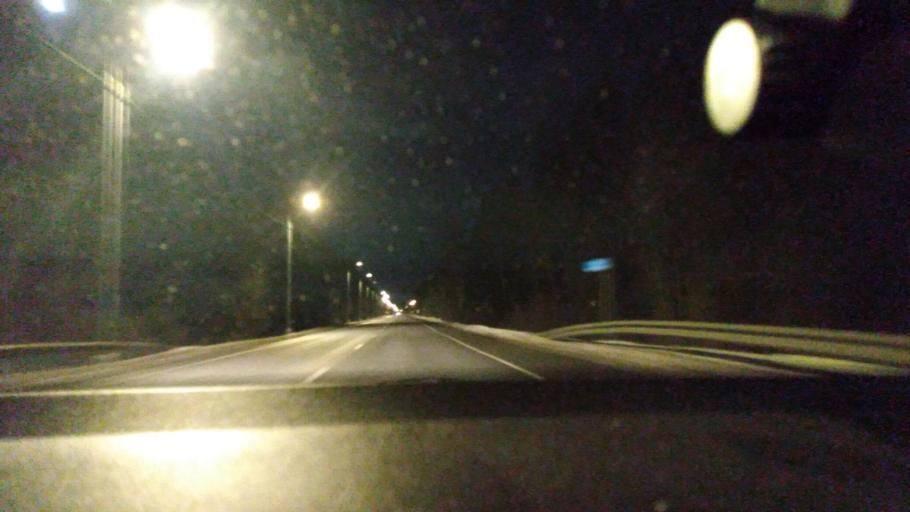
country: RU
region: Moskovskaya
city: Il'inskiy Pogost
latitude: 55.4625
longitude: 38.9792
